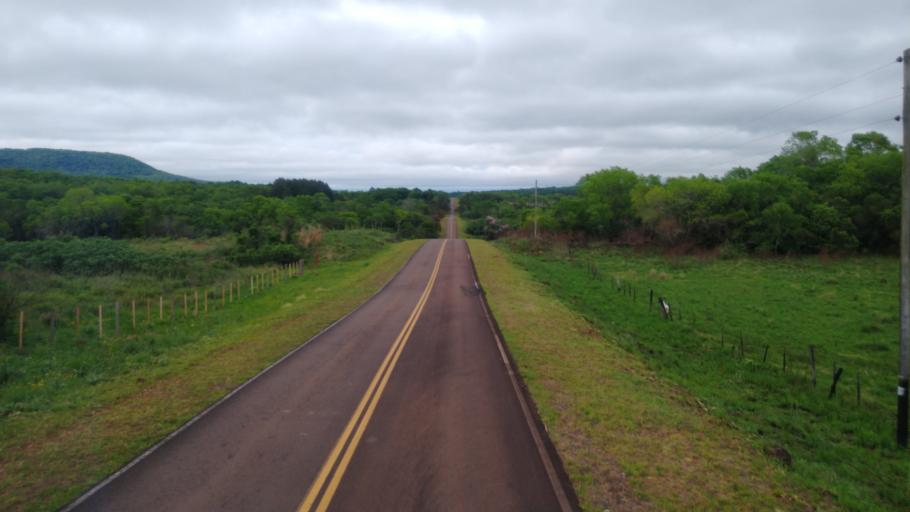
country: AR
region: Misiones
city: Santa Ana
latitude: -27.4117
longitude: -55.5587
